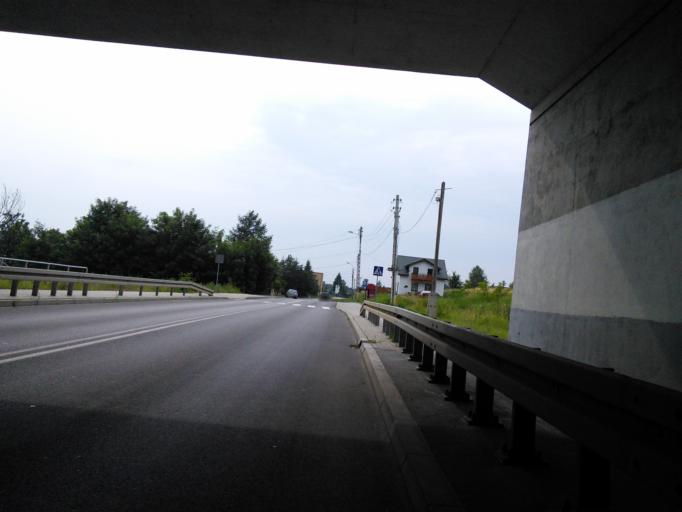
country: PL
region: Silesian Voivodeship
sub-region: Powiat bedzinski
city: Bobrowniki
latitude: 50.3756
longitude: 18.9662
